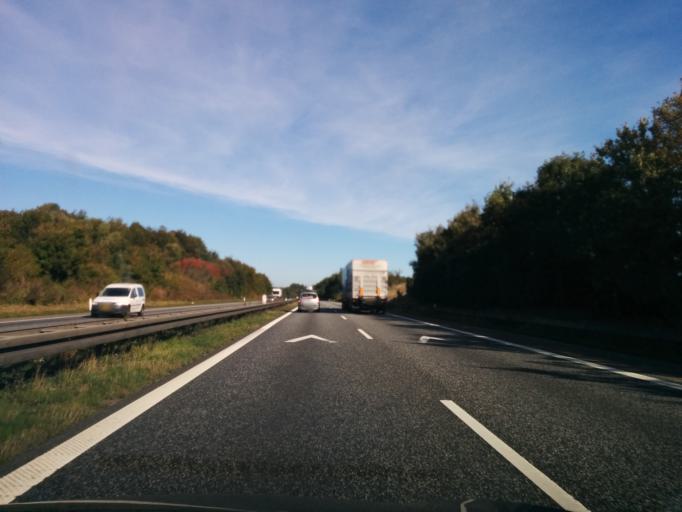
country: DK
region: Central Jutland
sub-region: Horsens Kommune
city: Horsens
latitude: 55.8662
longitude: 9.7651
